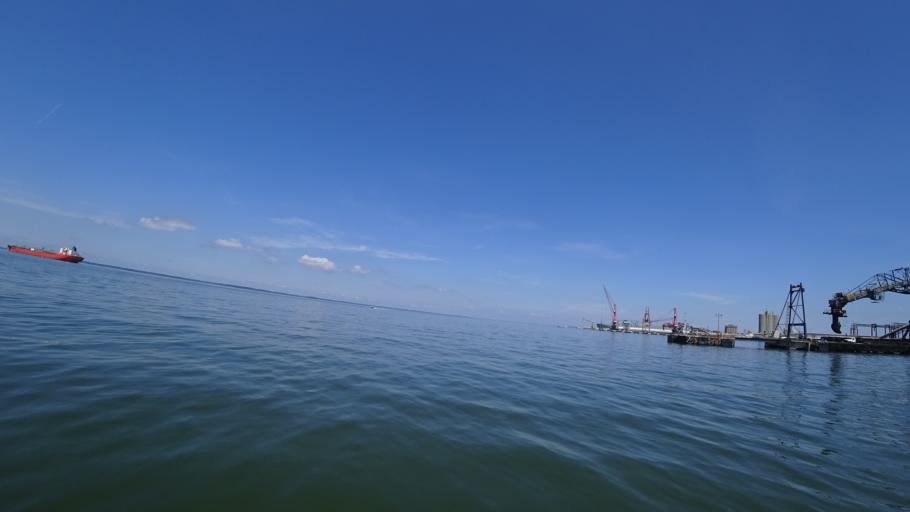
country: US
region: Virginia
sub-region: City of Newport News
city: Newport News
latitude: 36.9613
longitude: -76.4234
